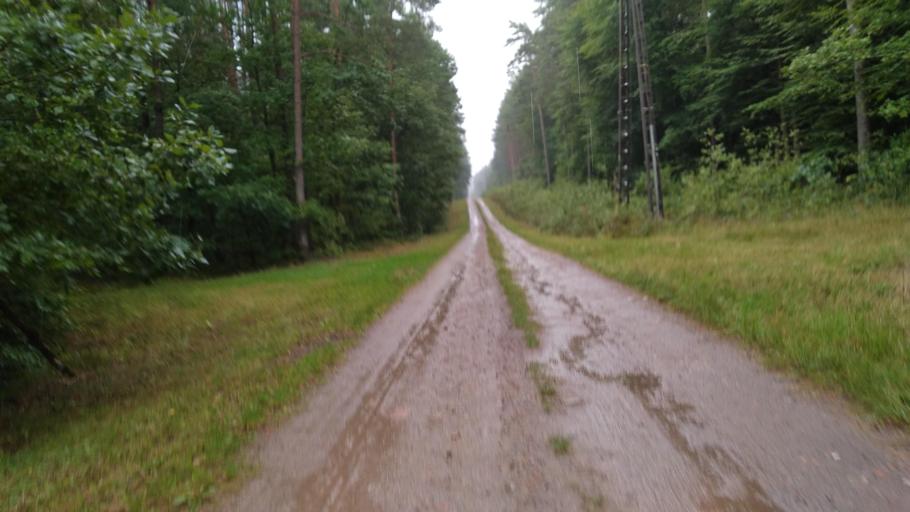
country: PL
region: Pomeranian Voivodeship
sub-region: Powiat wejherowski
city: Goscicino
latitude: 54.6252
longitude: 18.1444
